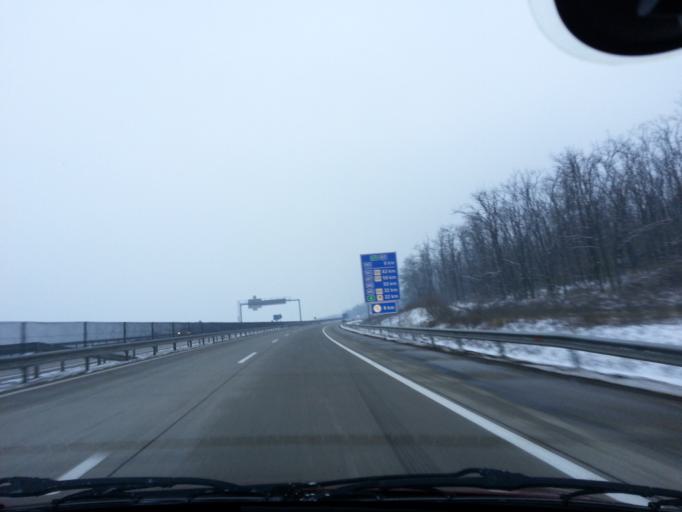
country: HU
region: Pest
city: Godollo
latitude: 47.5793
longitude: 19.3199
